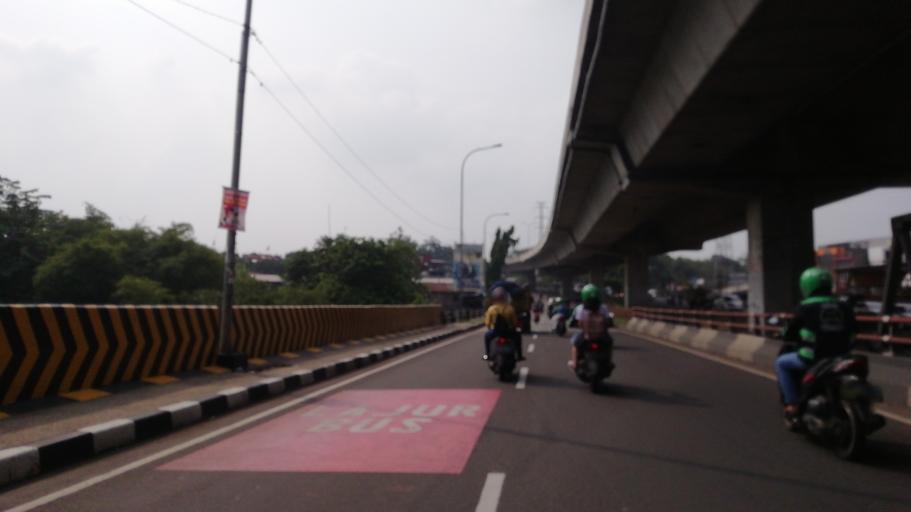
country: ID
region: West Java
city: Bogor
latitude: -6.5626
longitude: 106.8082
